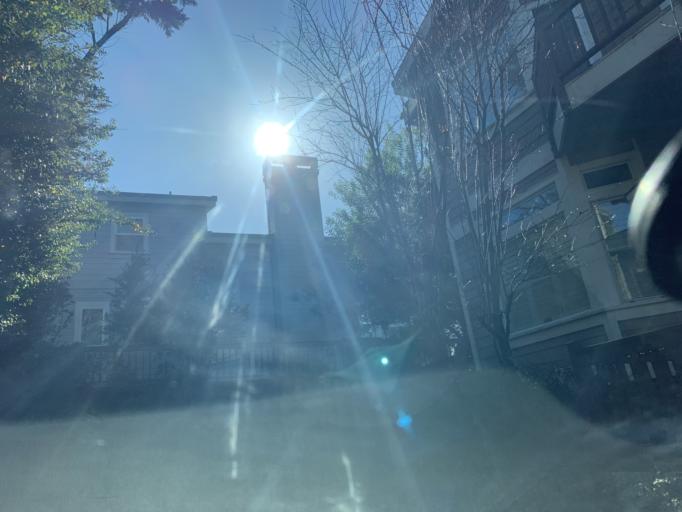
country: US
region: California
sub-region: Marin County
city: Strawberry
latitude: 37.9008
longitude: -122.5127
